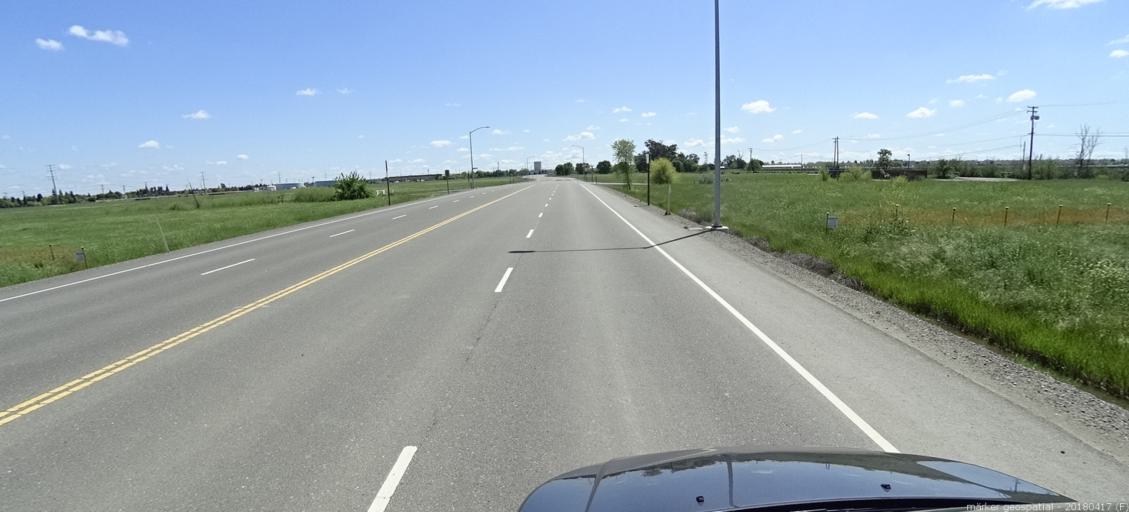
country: US
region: California
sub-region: Sacramento County
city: Laguna
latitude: 38.4384
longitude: -121.4630
